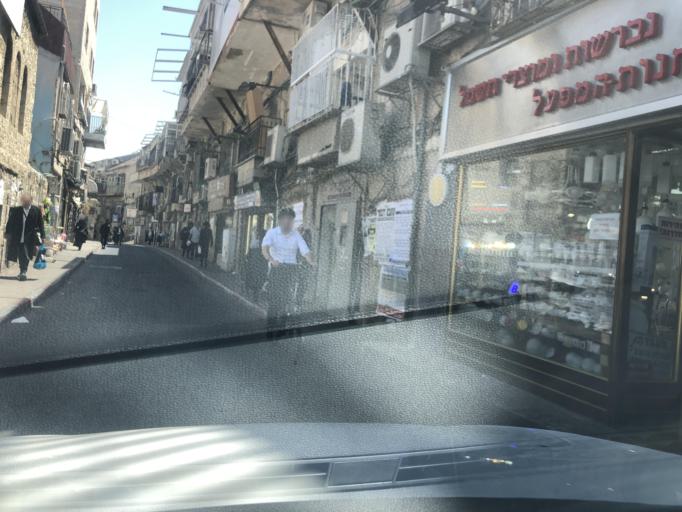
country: IL
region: Jerusalem
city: West Jerusalem
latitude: 31.7879
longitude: 35.2207
